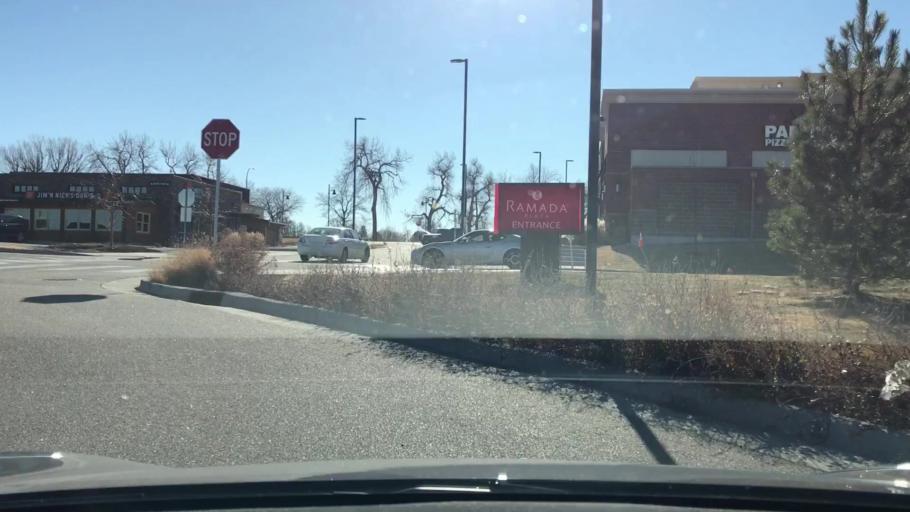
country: US
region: Colorado
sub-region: Adams County
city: Northglenn
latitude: 39.9129
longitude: -104.9867
